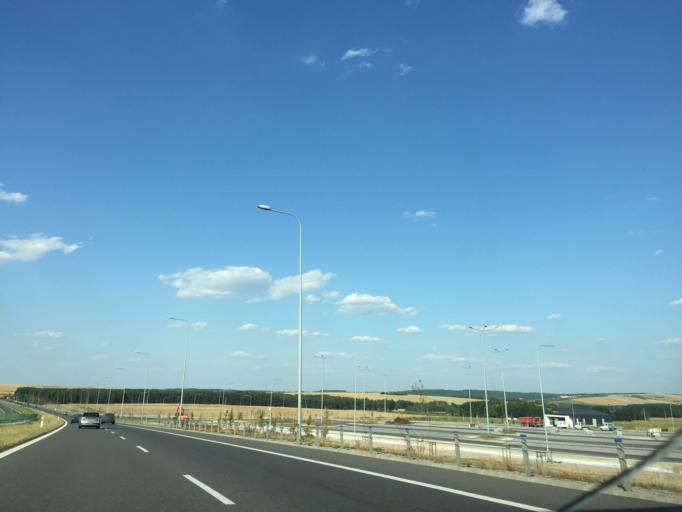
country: PL
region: Swietokrzyskie
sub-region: Powiat jedrzejowski
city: Sobkow
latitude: 50.7024
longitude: 20.3999
